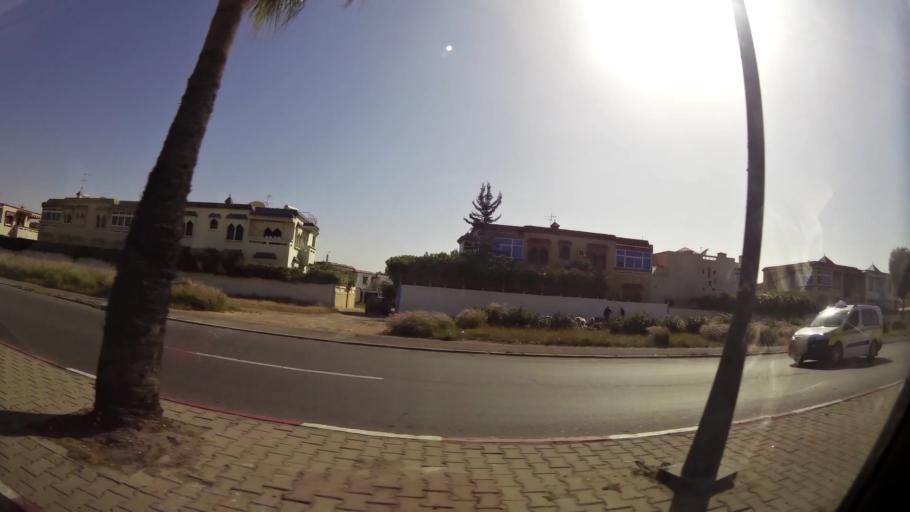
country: MA
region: Souss-Massa-Draa
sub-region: Inezgane-Ait Mellou
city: Inezgane
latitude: 30.3777
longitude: -9.5599
